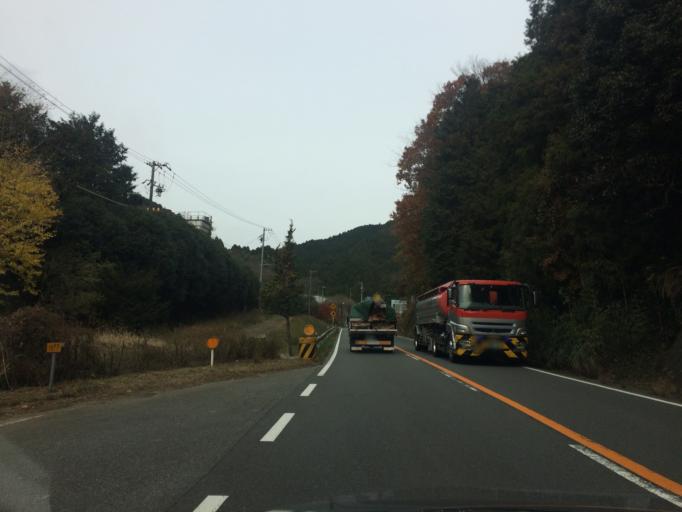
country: JP
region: Shizuoka
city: Fujinomiya
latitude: 35.1767
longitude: 138.5231
